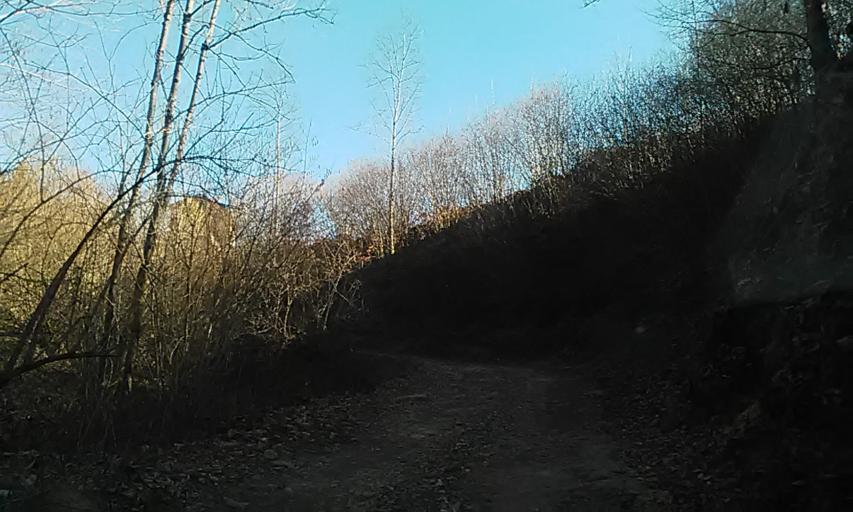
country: IT
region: Piedmont
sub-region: Provincia di Vercelli
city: Civiasco
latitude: 45.8124
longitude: 8.3064
